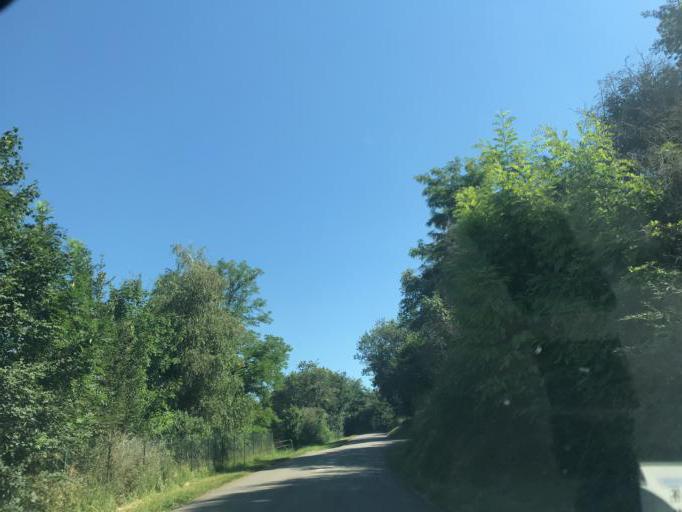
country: FR
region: Rhone-Alpes
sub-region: Departement de l'Ain
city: Saint-Martin-du-Mont
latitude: 46.0986
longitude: 5.3209
